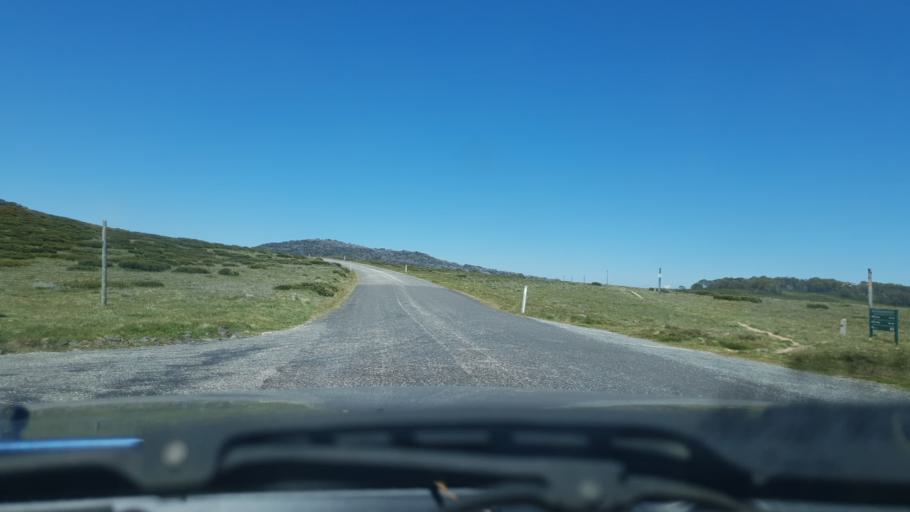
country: AU
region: Victoria
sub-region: Alpine
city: Mount Beauty
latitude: -36.9055
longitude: 147.2893
